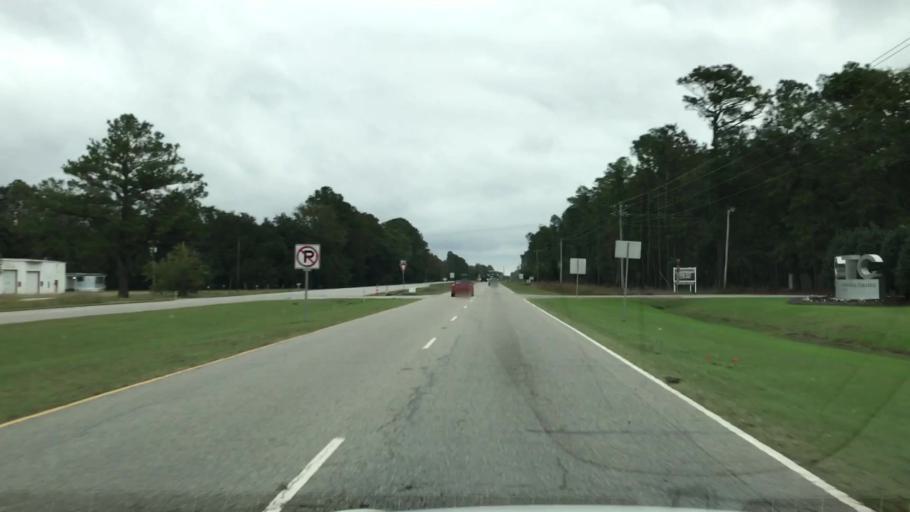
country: US
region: South Carolina
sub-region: Georgetown County
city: Georgetown
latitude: 33.3209
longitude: -79.3217
